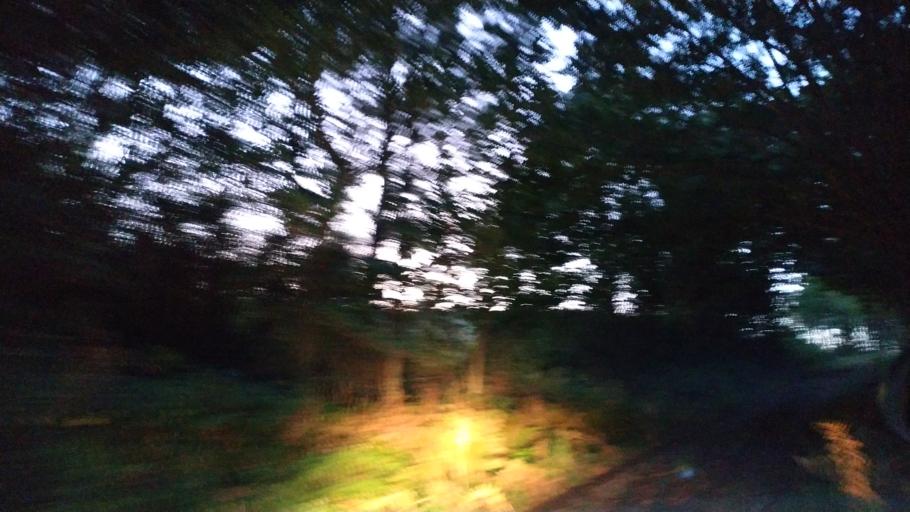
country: ES
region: Galicia
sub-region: Provincia da Coruna
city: Negreira
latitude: 42.9149
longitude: -8.7580
